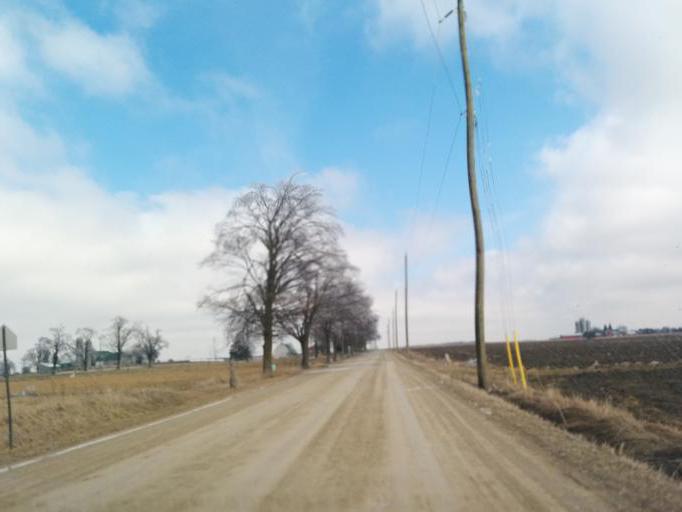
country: CA
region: Ontario
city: Waterloo
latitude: 43.6228
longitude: -80.5423
